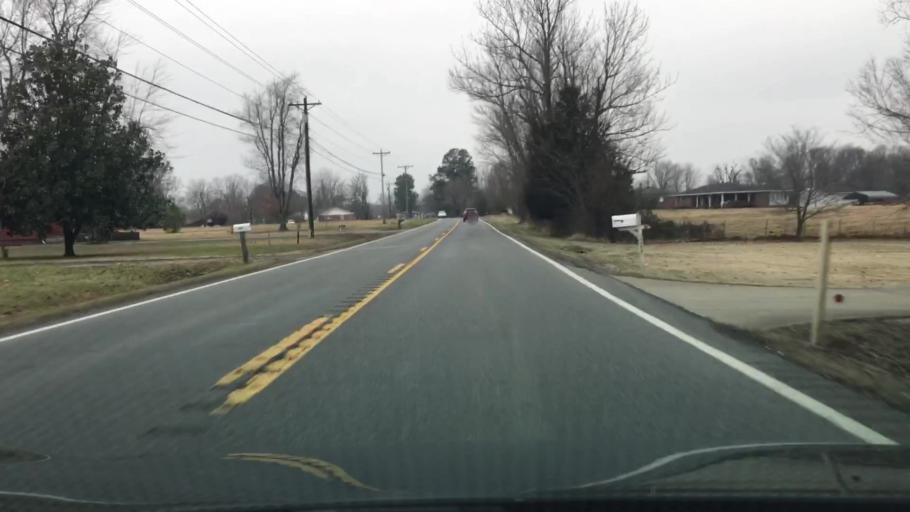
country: US
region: Kentucky
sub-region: Marshall County
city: Calvert City
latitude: 36.9706
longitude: -88.3903
